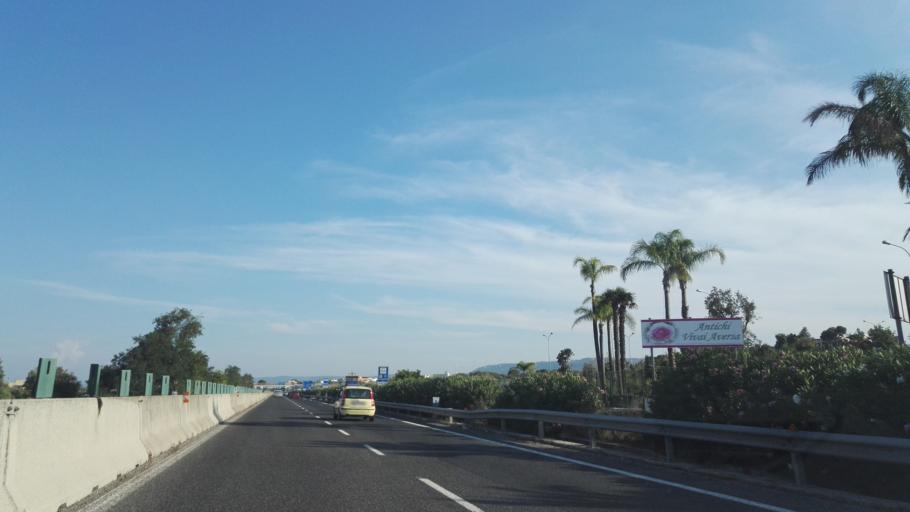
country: IT
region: Apulia
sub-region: Provincia di Bari
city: Monopoli
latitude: 40.9005
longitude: 17.3277
